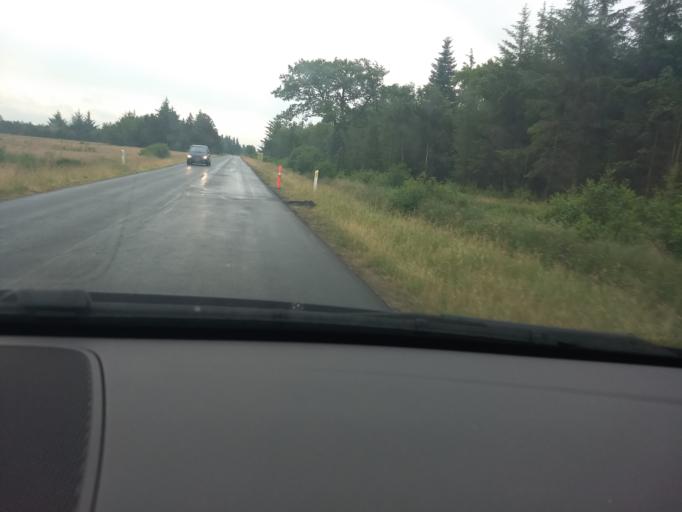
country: DK
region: South Denmark
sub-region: Fano Kommune
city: Nordby
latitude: 55.3789
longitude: 8.4460
